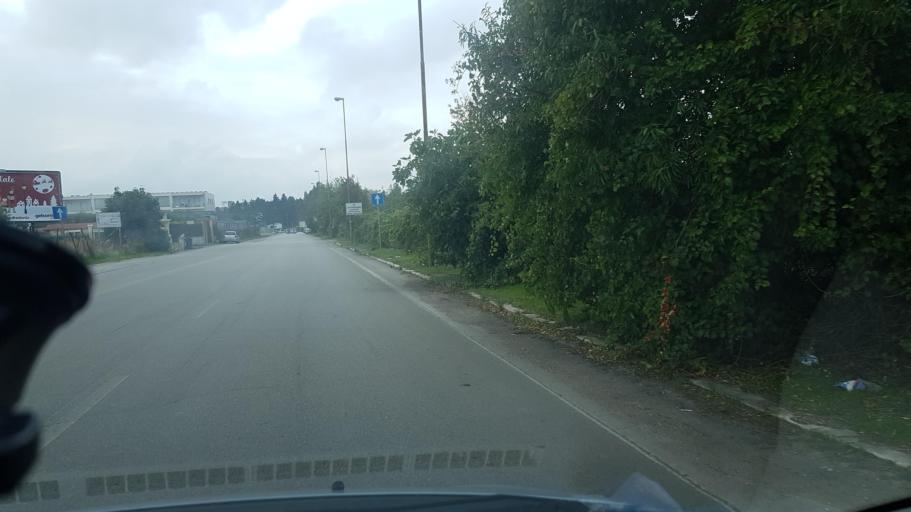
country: IT
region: Apulia
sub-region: Provincia di Foggia
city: Foggia
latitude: 41.4759
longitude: 15.5518
